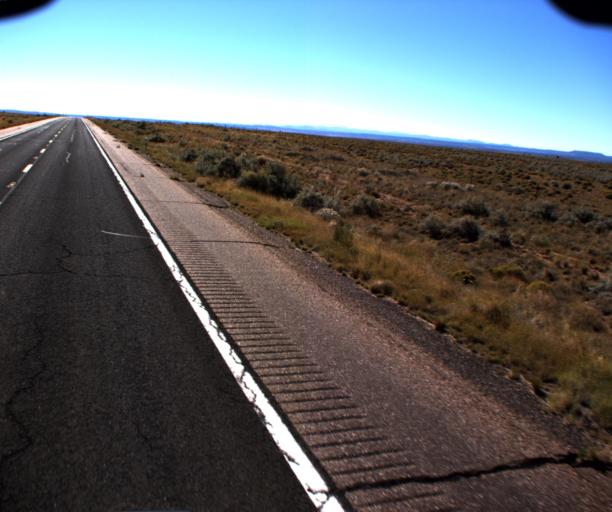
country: US
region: Arizona
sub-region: Navajo County
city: Snowflake
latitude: 34.7097
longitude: -109.7621
